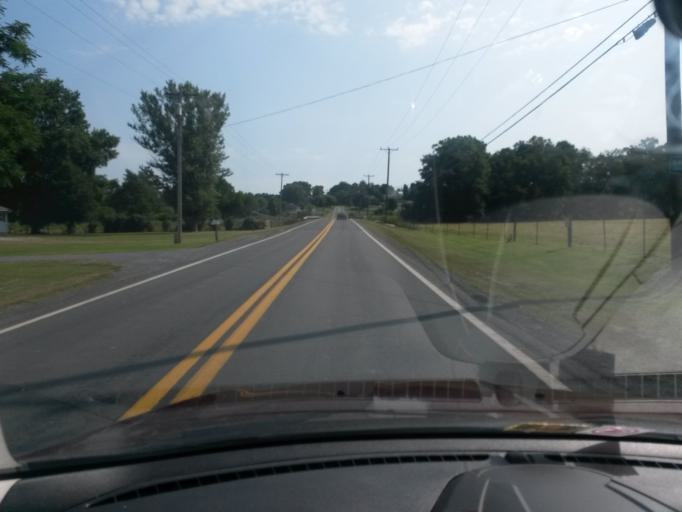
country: US
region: Virginia
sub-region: Shenandoah County
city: Basye
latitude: 38.9262
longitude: -78.8389
